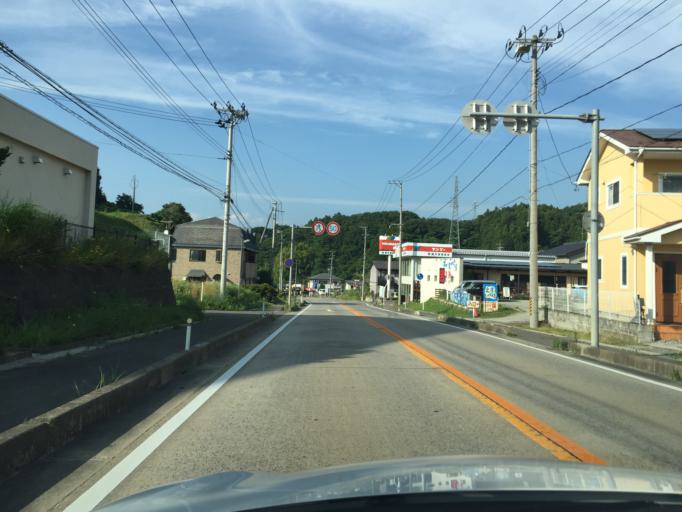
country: JP
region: Fukushima
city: Miharu
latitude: 37.4357
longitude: 140.5003
